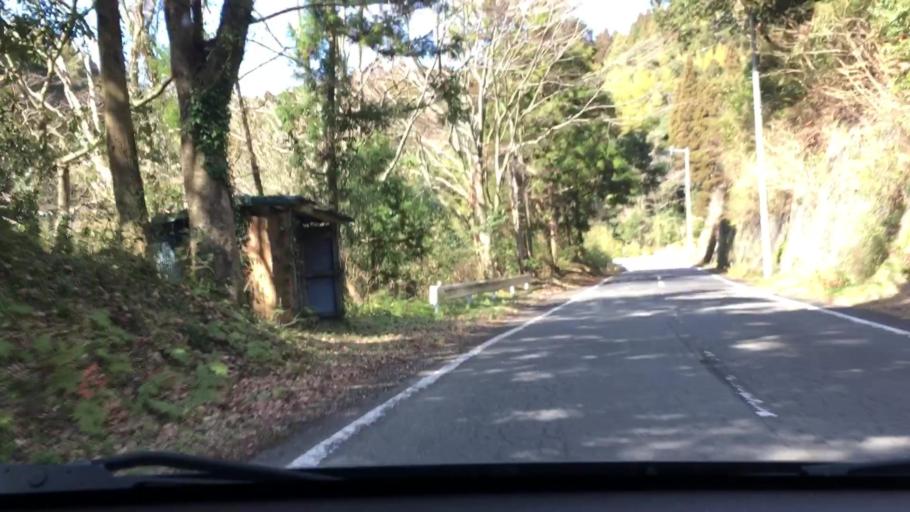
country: JP
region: Kagoshima
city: Ijuin
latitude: 31.7125
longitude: 130.4173
